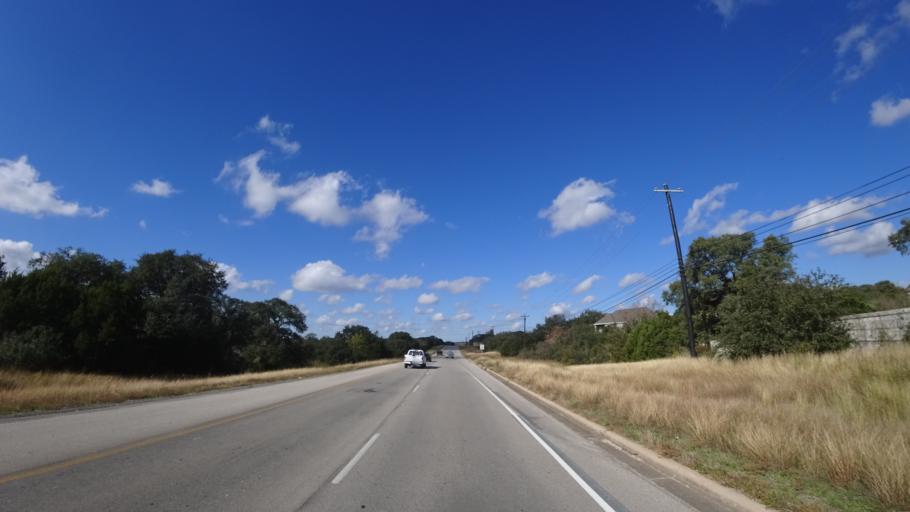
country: US
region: Texas
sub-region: Travis County
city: Shady Hollow
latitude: 30.1832
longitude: -97.9023
